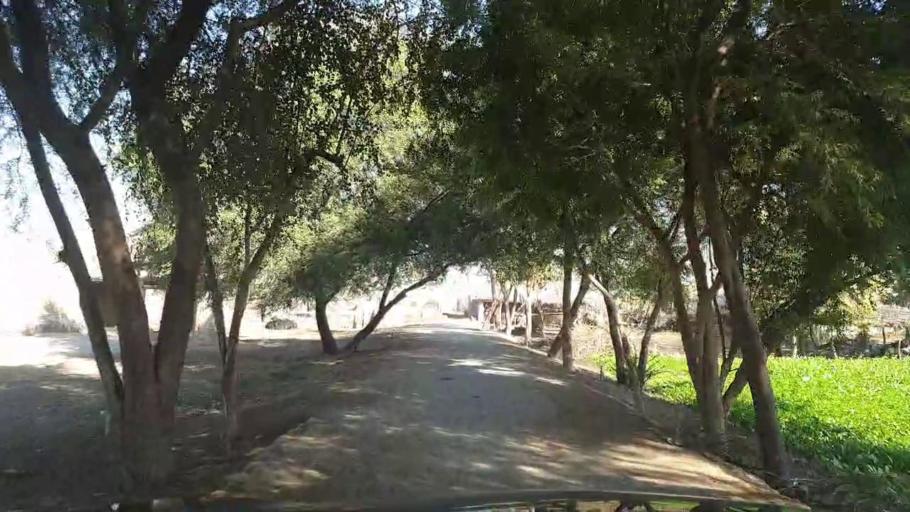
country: PK
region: Sindh
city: Ghotki
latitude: 27.9998
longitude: 69.3429
